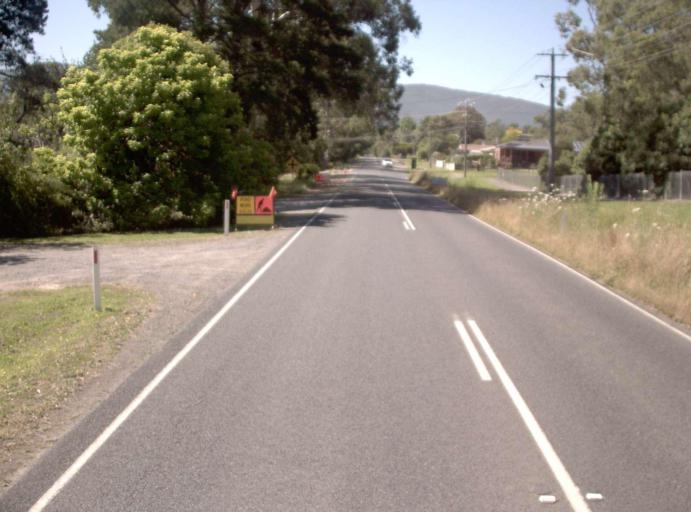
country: AU
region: Victoria
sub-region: Yarra Ranges
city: Healesville
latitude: -37.6599
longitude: 145.5297
